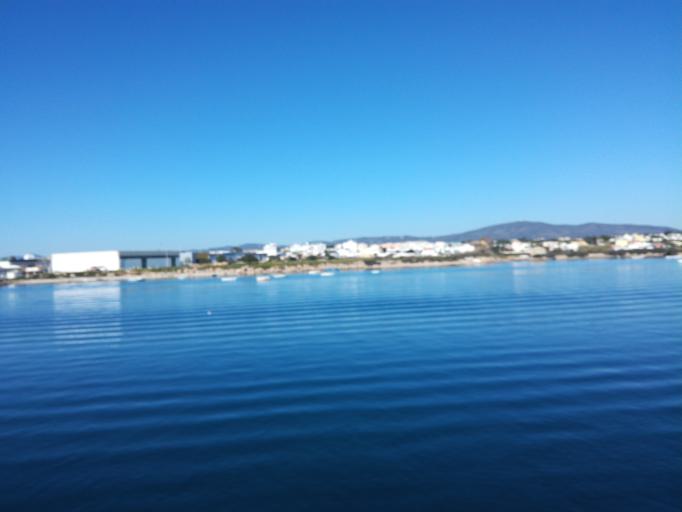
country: PT
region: Faro
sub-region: Olhao
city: Olhao
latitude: 37.0265
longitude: -7.8252
